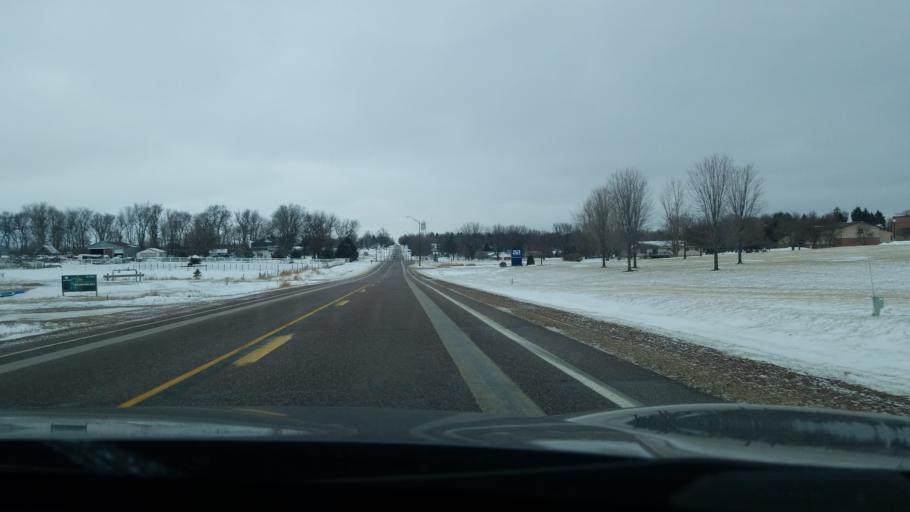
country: US
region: Iowa
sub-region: Lyon County
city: Rock Rapids
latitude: 43.4162
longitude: -96.1758
